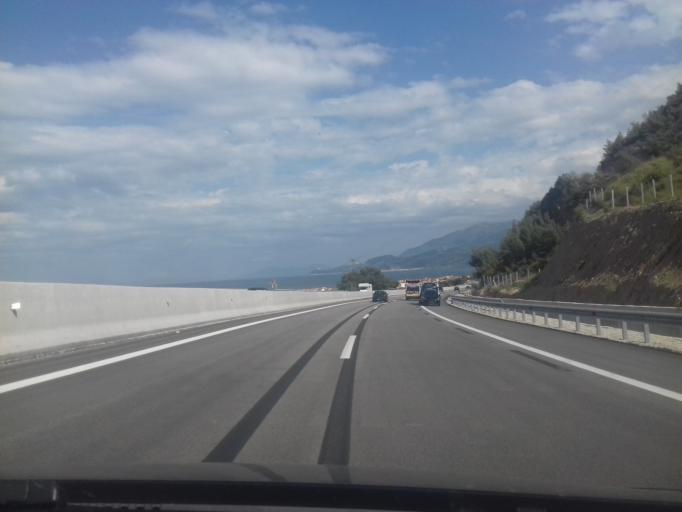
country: GR
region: West Greece
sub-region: Nomos Achaias
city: Siliveniotika
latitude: 38.1703
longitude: 22.3223
